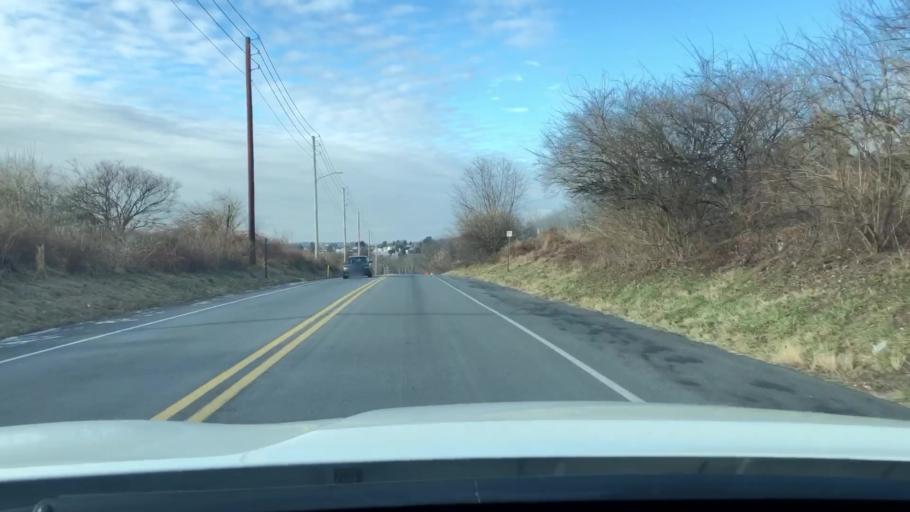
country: US
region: Pennsylvania
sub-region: Lehigh County
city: Fullerton
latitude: 40.6402
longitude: -75.4556
